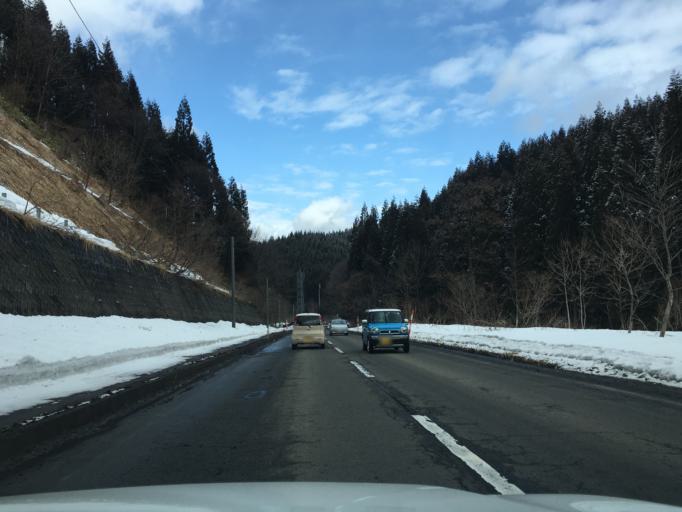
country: JP
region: Akita
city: Takanosu
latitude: 39.9882
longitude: 140.2462
